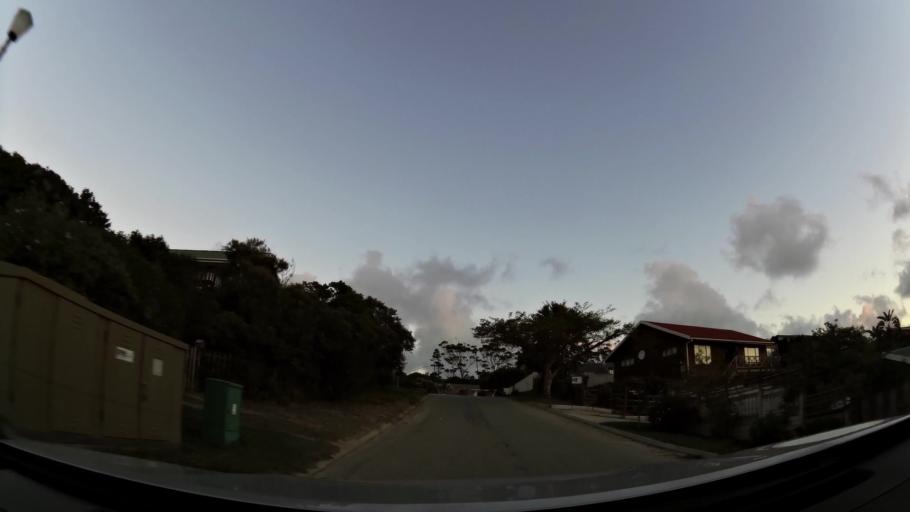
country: ZA
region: Western Cape
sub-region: Eden District Municipality
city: Knysna
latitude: -34.0277
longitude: 22.8097
